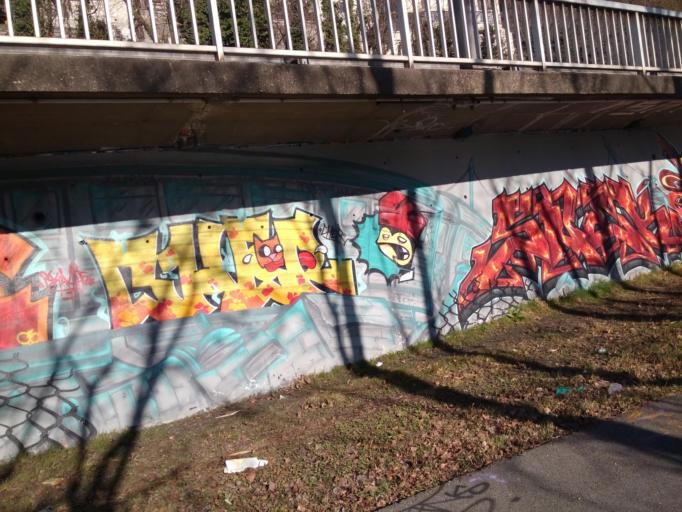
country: FR
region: Rhone-Alpes
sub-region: Departement de l'Isere
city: Saint-Martin-le-Vinoux
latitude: 45.2024
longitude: 5.7145
